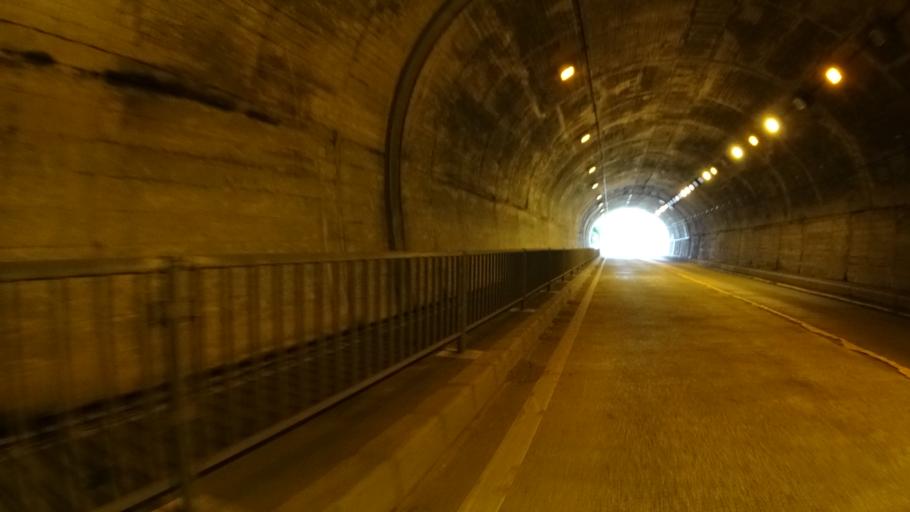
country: JP
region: Kanagawa
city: Yokosuka
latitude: 35.2144
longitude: 139.7116
